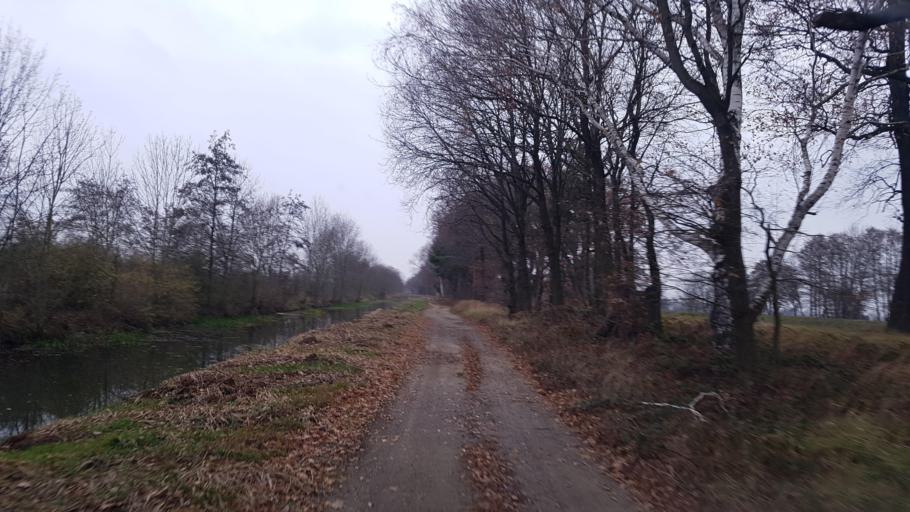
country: DE
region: Brandenburg
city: Hirschfeld
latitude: 51.4107
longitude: 13.6313
